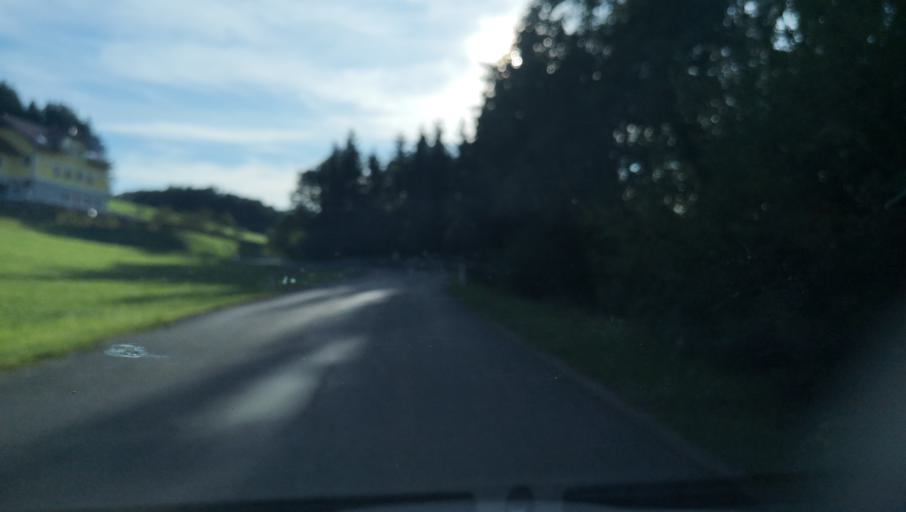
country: AT
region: Lower Austria
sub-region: Politischer Bezirk Amstetten
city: Neuhofen an der Ybbs
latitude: 47.9975
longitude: 14.8722
